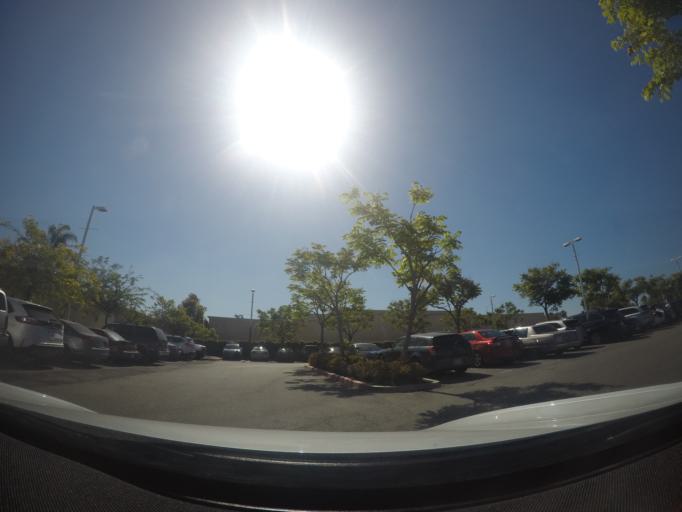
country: US
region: California
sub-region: Los Angeles County
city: Torrance
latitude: 33.8393
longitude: -118.3562
